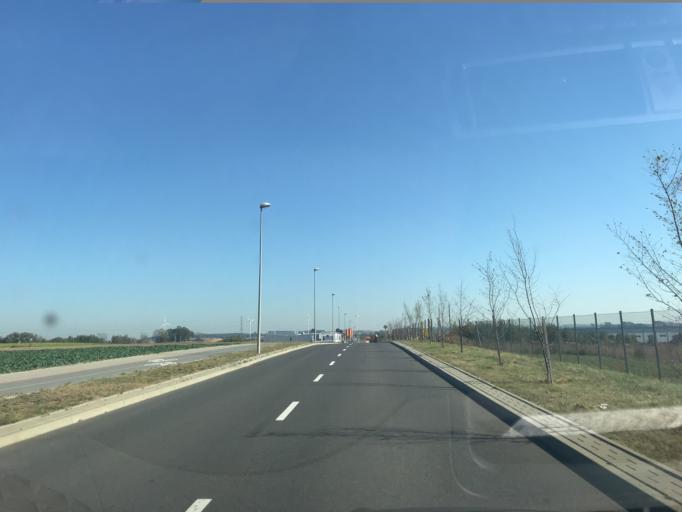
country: PL
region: Warmian-Masurian Voivodeship
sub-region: Powiat ilawski
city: Lubawa
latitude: 53.5160
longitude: 19.7265
